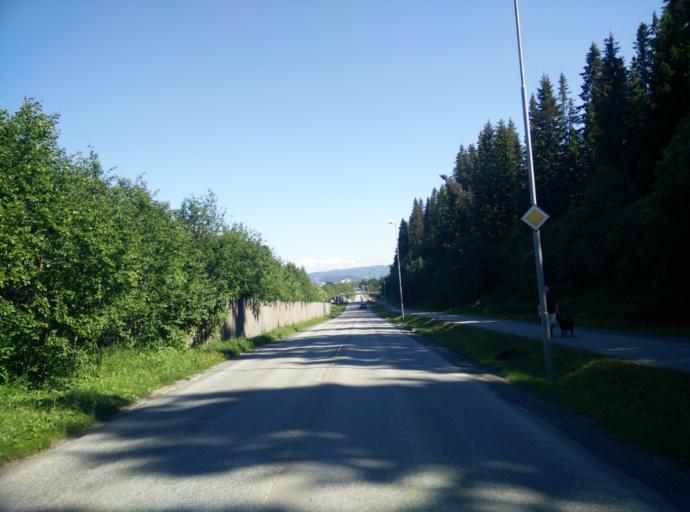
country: NO
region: Sor-Trondelag
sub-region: Trondheim
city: Trondheim
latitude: 63.3752
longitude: 10.3237
